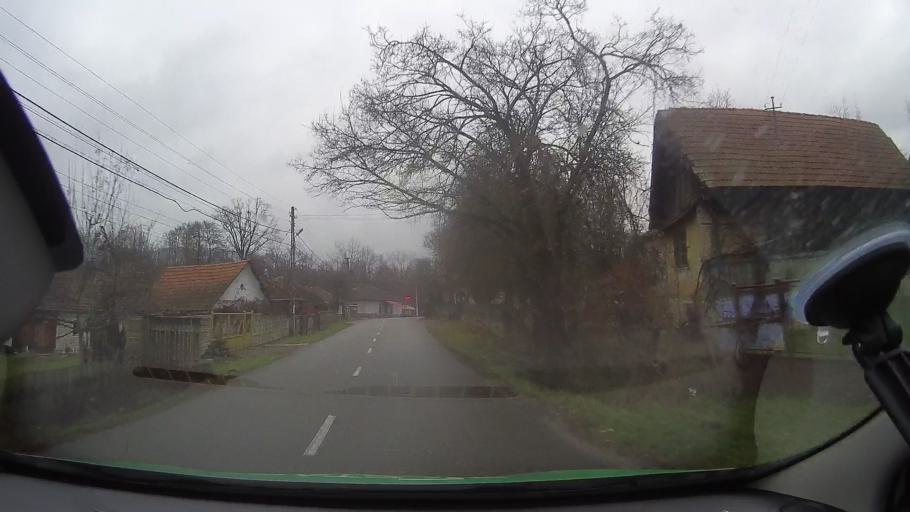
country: RO
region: Hunedoara
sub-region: Comuna Tomesti
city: Tomesti
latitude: 46.2130
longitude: 22.6651
